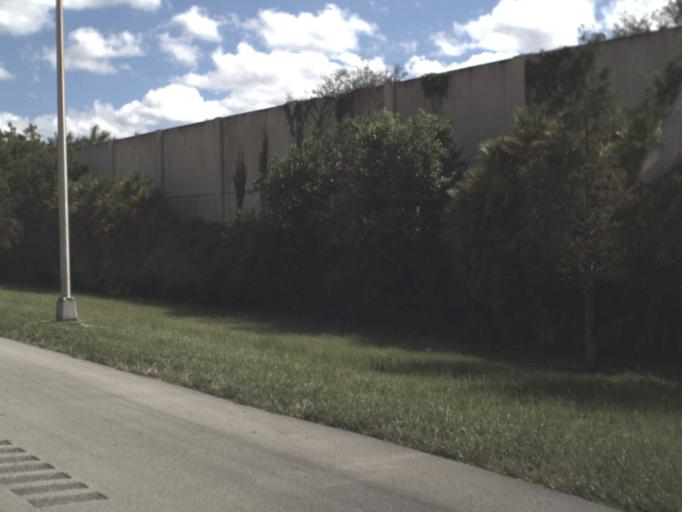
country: US
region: Florida
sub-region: Broward County
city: Parkland
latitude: 26.3004
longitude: -80.2164
